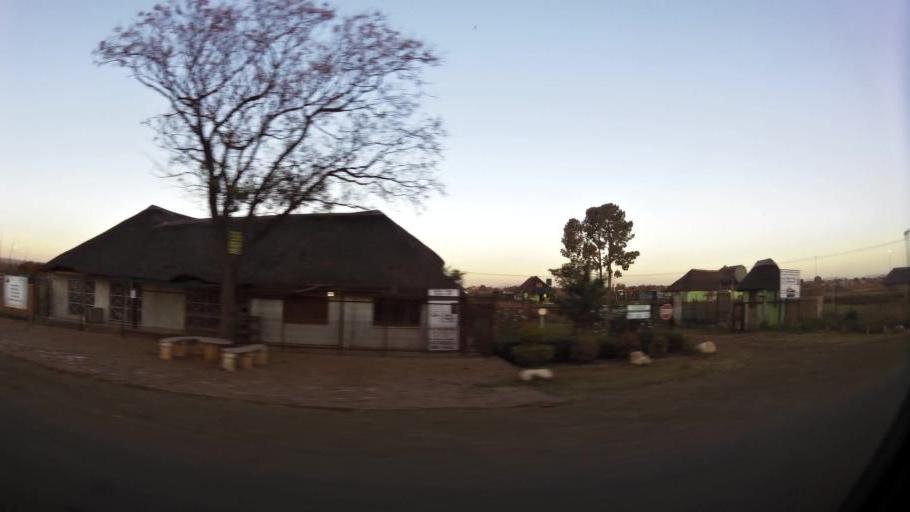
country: ZA
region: North-West
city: Ga-Rankuwa
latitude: -25.5790
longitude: 28.0487
